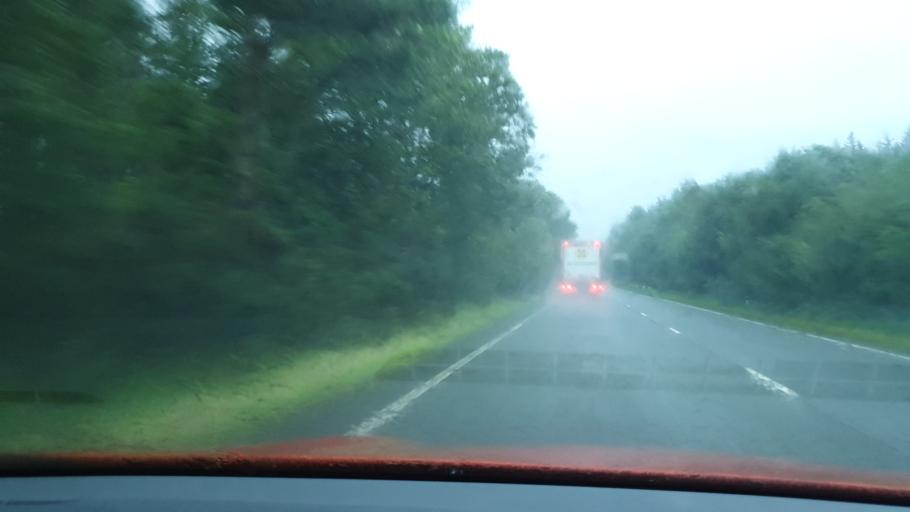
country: GB
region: England
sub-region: Cumbria
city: Ulverston
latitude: 54.2500
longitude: -3.0262
